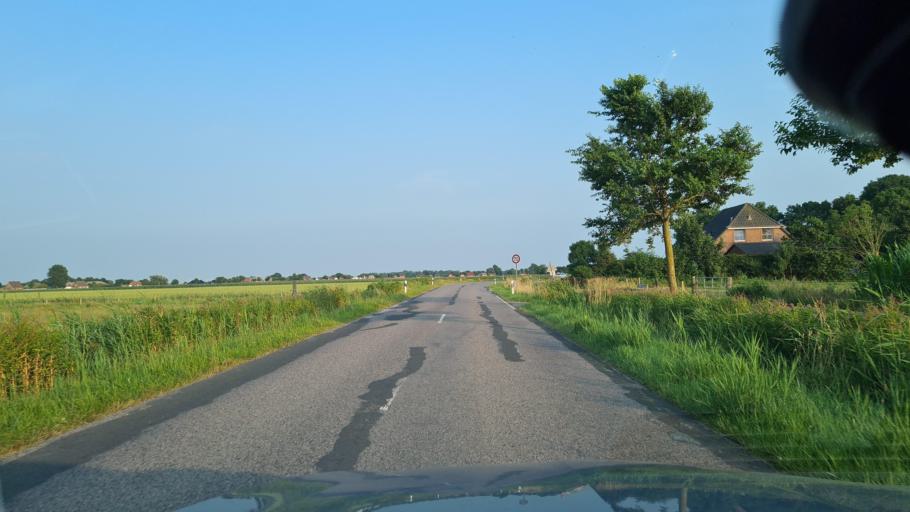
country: DE
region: Schleswig-Holstein
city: Elisabeth-Sophien-Koog
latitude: 54.4946
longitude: 8.8482
